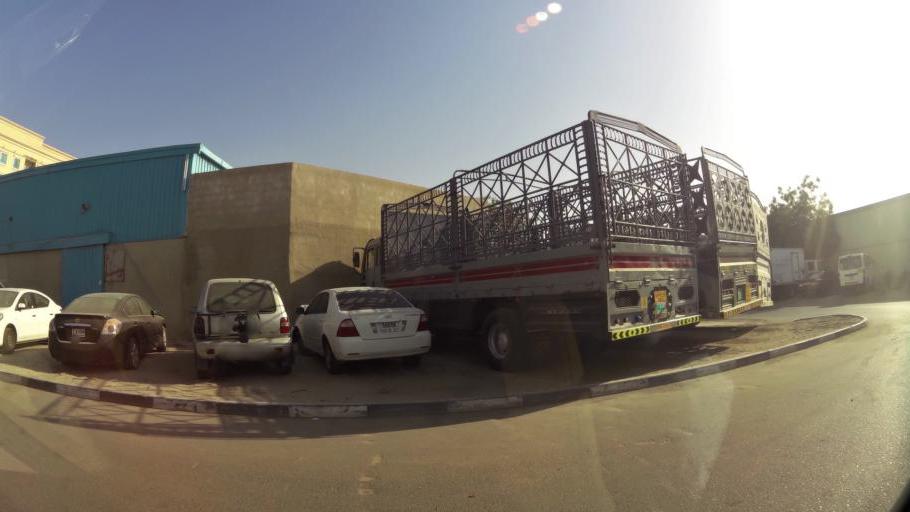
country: AE
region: Ash Shariqah
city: Sharjah
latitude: 25.2865
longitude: 55.3888
